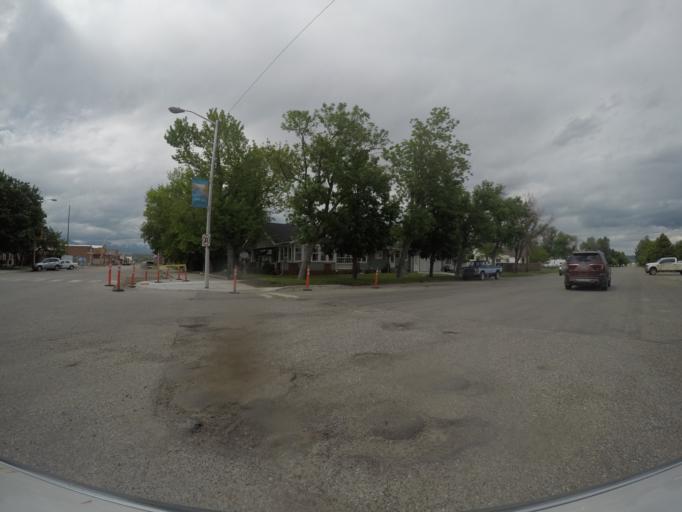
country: US
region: Montana
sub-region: Sweet Grass County
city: Big Timber
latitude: 45.8326
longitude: -109.9524
